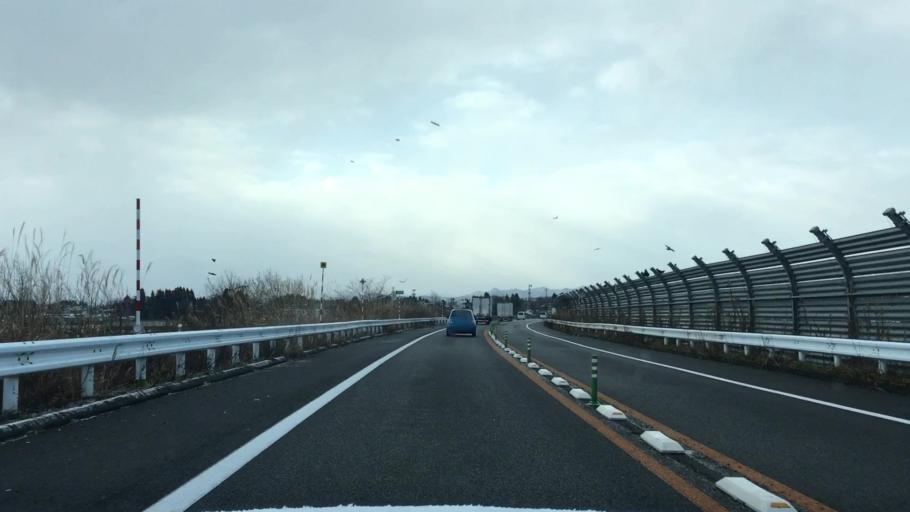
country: JP
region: Akita
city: Odate
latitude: 40.2844
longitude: 140.5407
